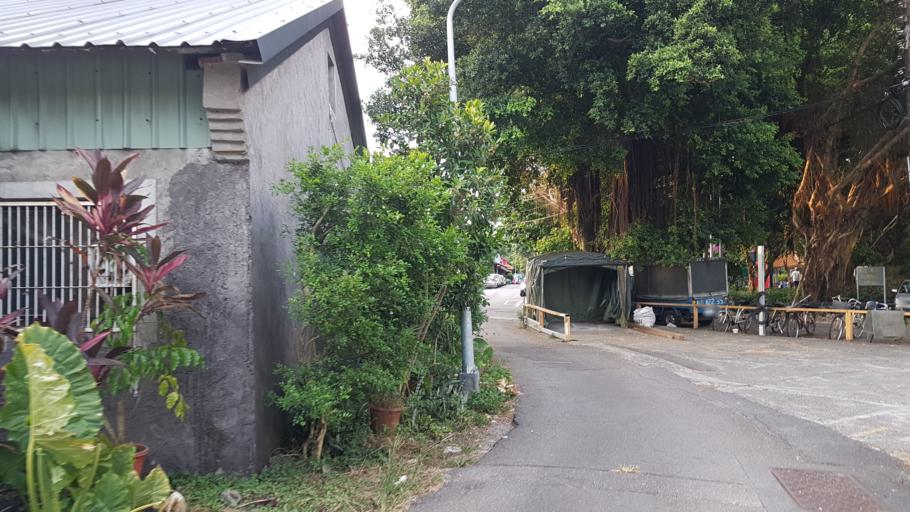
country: TW
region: Taipei
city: Taipei
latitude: 25.0236
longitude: 121.5602
